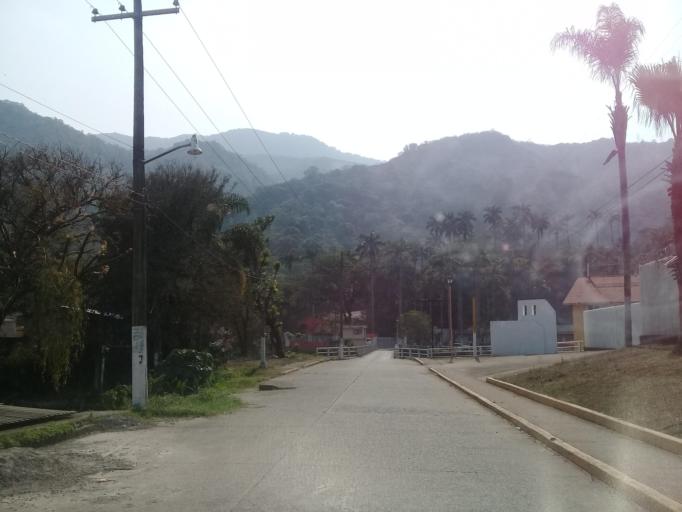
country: MX
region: Veracruz
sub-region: Ixtaczoquitlan
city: Campo Chico
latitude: 18.8370
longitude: -97.0326
